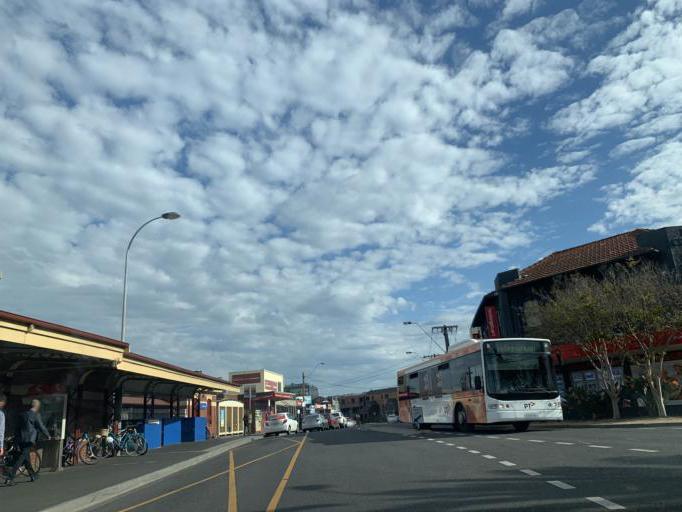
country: AU
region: Victoria
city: Hampton
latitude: -37.9503
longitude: 145.0043
